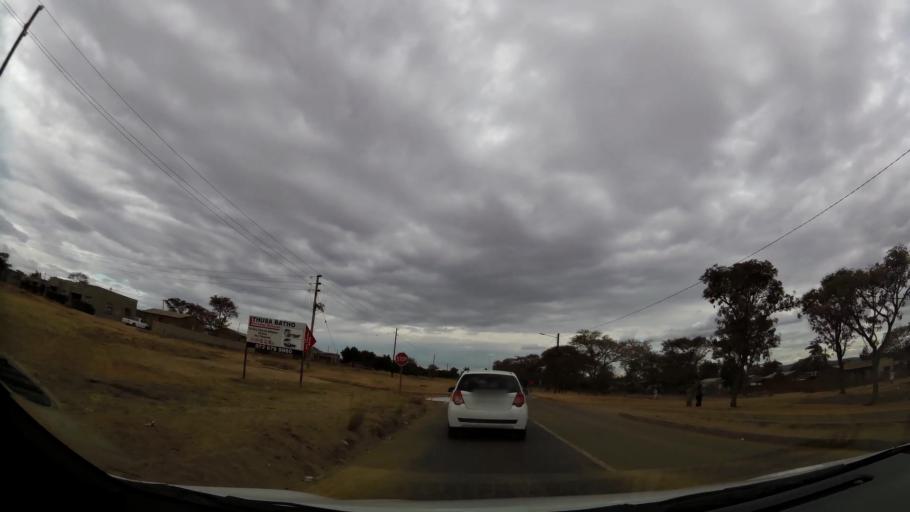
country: ZA
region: Limpopo
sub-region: Waterberg District Municipality
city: Modimolle
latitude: -24.6974
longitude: 28.4242
